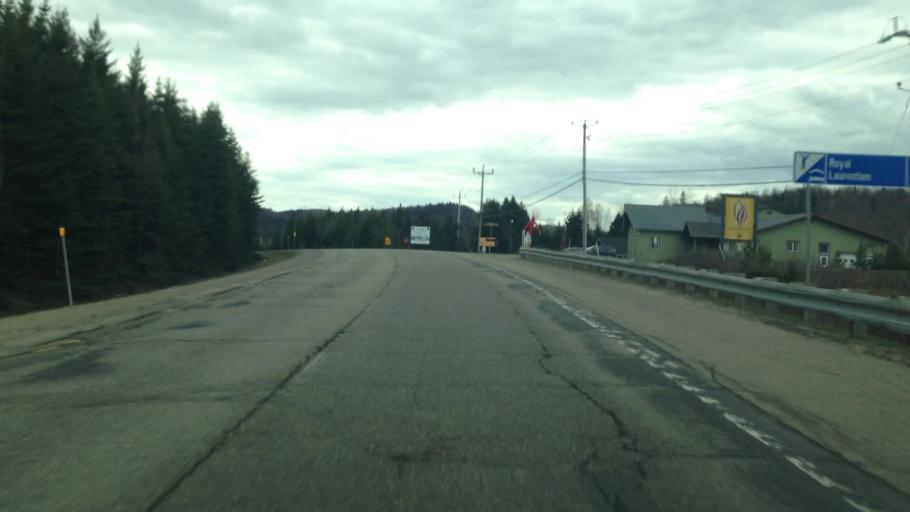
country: CA
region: Quebec
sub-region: Laurentides
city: Sainte-Agathe-des-Monts
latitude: 46.1046
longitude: -74.3987
